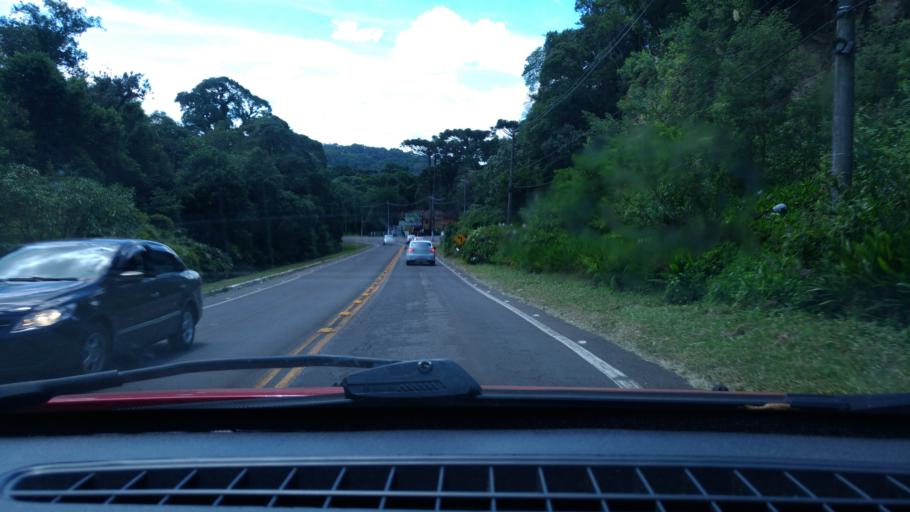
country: BR
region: Rio Grande do Sul
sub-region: Canela
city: Canela
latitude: -29.3518
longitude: -50.8323
